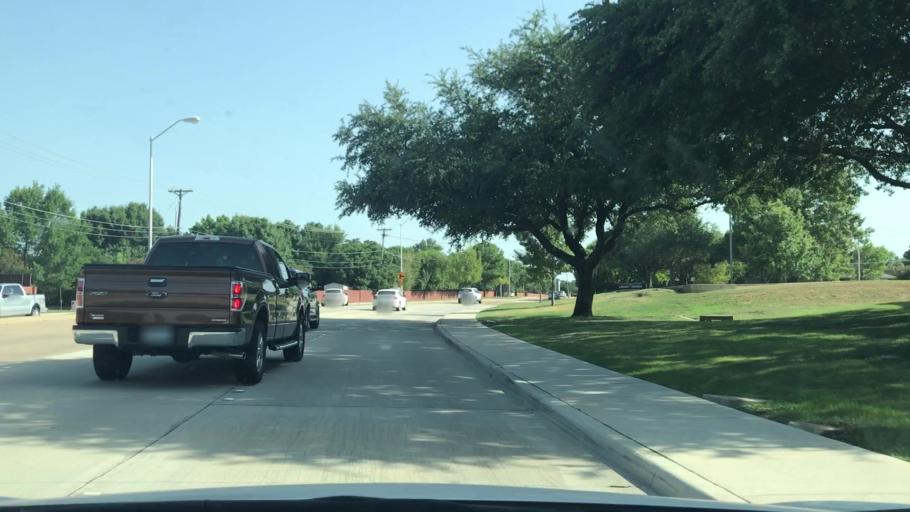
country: US
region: Texas
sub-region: Collin County
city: Plano
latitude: 33.0540
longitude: -96.7506
